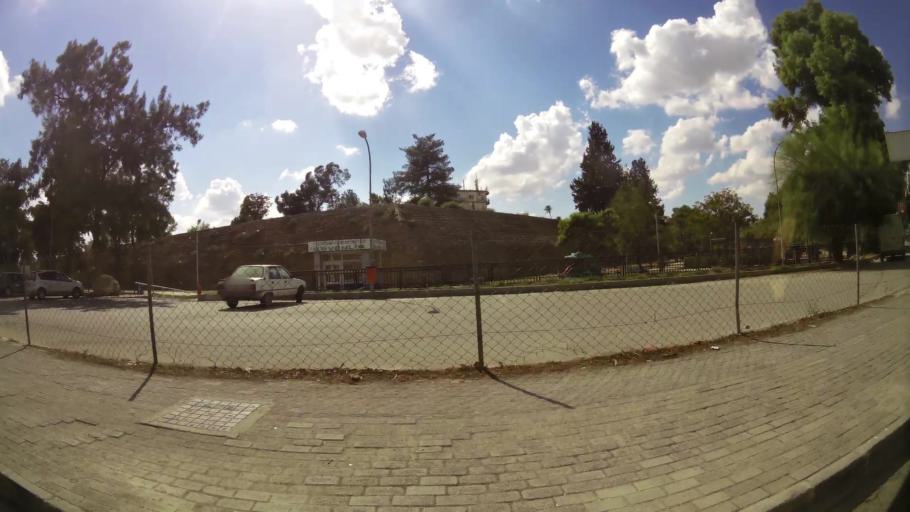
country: CY
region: Lefkosia
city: Nicosia
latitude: 35.1820
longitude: 33.3690
